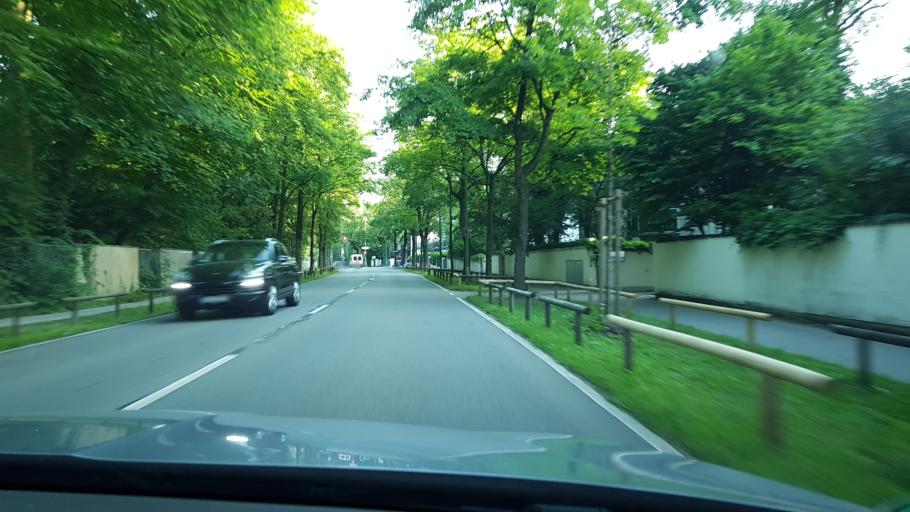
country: DE
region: Bavaria
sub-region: Upper Bavaria
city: Bogenhausen
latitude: 48.1655
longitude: 11.6228
